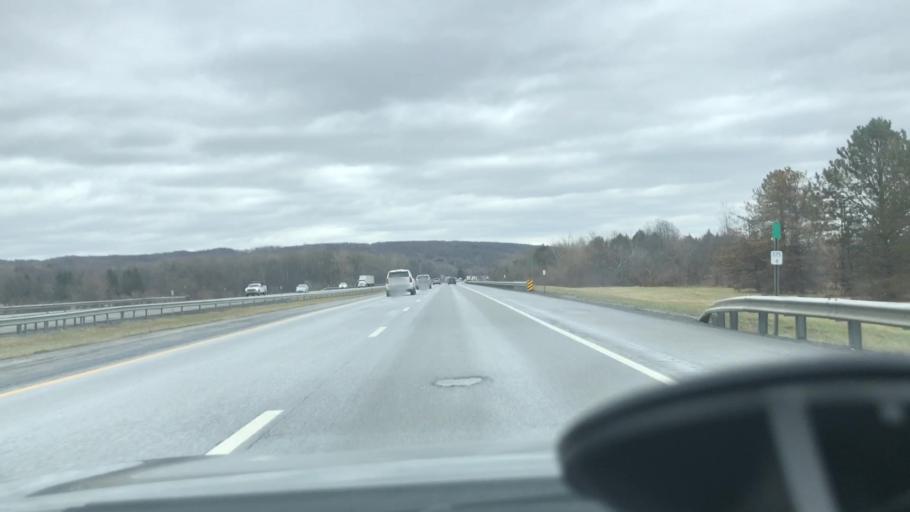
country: US
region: New York
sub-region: Herkimer County
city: Frankfort
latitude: 43.0615
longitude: -75.0776
